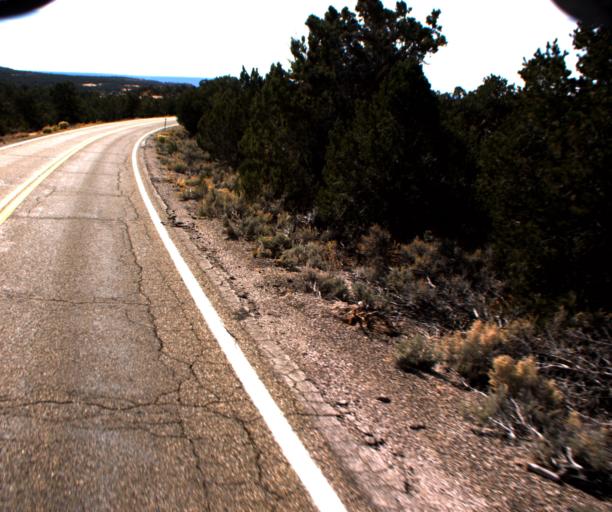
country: US
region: Arizona
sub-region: Navajo County
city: Kayenta
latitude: 36.6627
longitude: -110.5267
